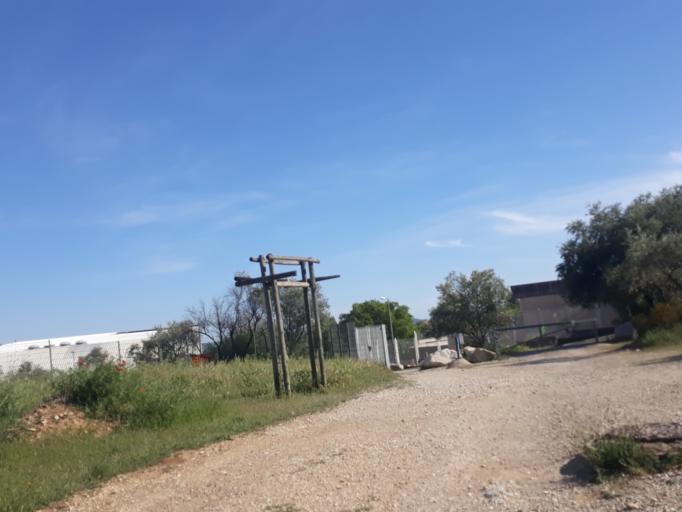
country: FR
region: Languedoc-Roussillon
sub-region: Departement du Gard
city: Nimes
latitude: 43.8205
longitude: 4.3284
